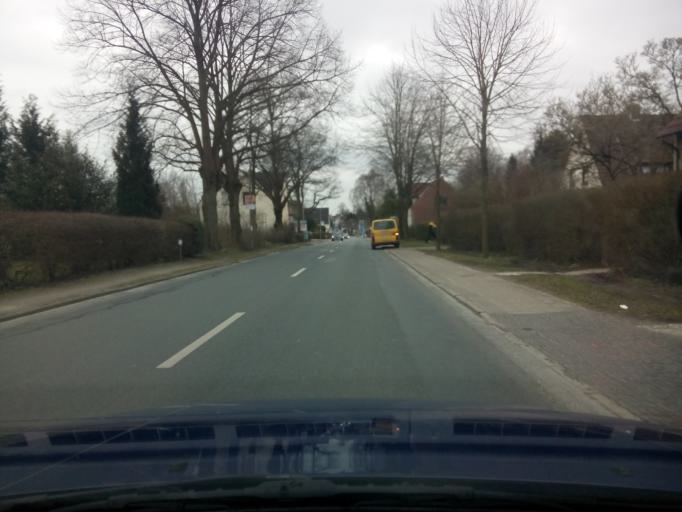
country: DE
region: Lower Saxony
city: Osterholz-Scharmbeck
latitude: 53.2303
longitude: 8.8099
